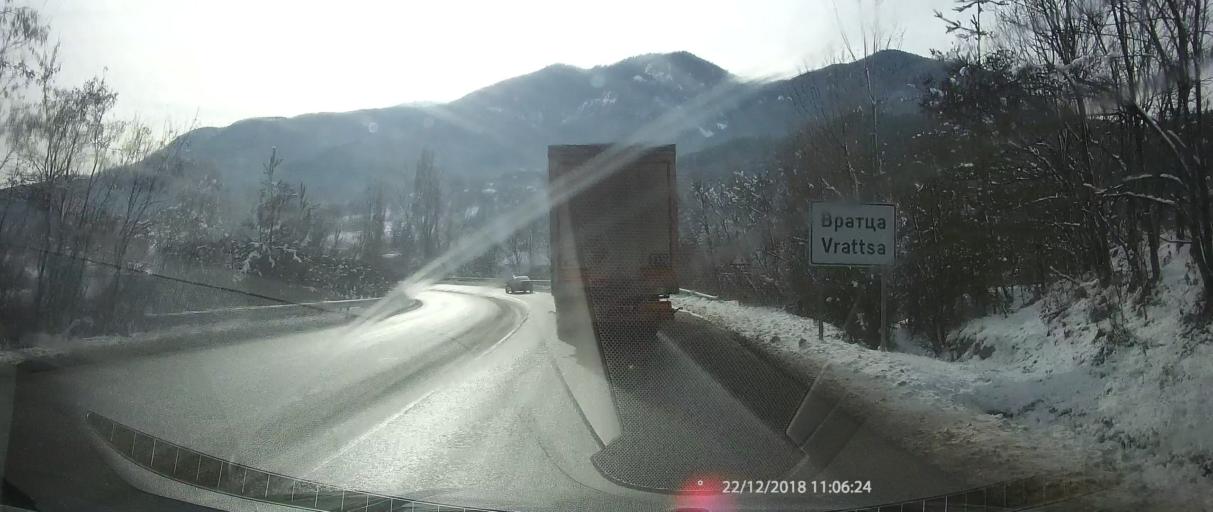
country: BG
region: Kyustendil
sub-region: Obshtina Kyustendil
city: Kyustendil
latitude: 42.2641
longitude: 22.5837
